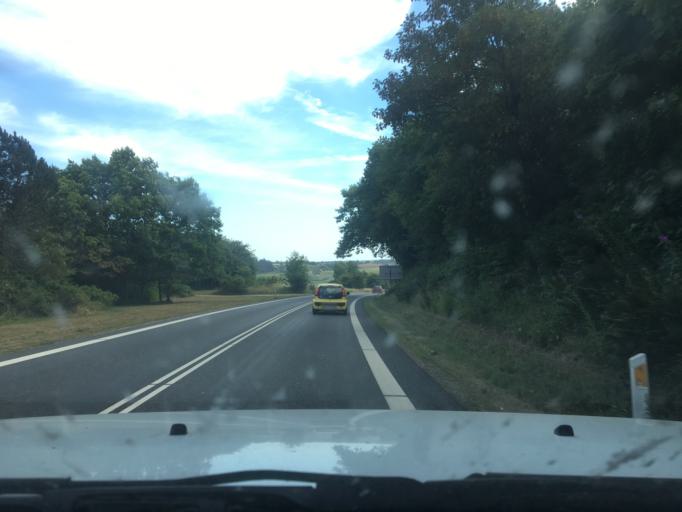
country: DK
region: Central Jutland
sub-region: Viborg Kommune
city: Viborg
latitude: 56.5782
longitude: 9.3765
